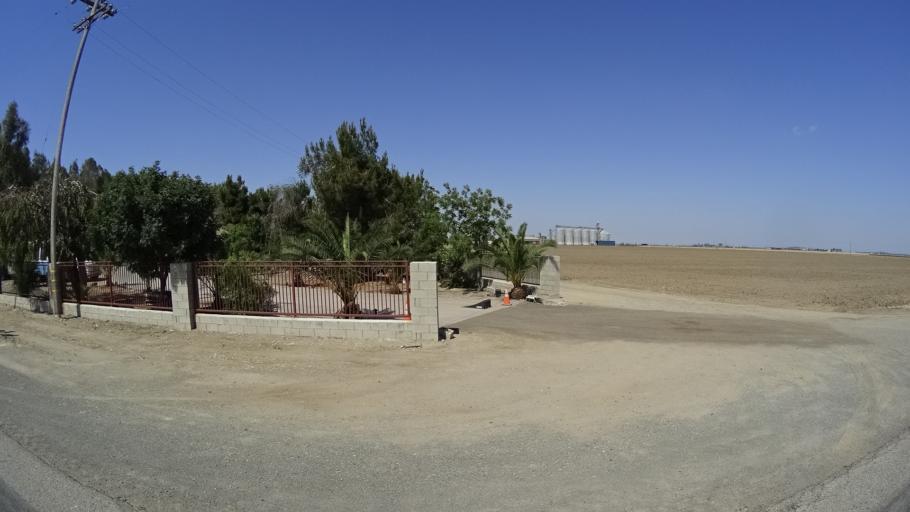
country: US
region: California
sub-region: Kings County
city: Home Garden
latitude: 36.2159
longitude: -119.6368
